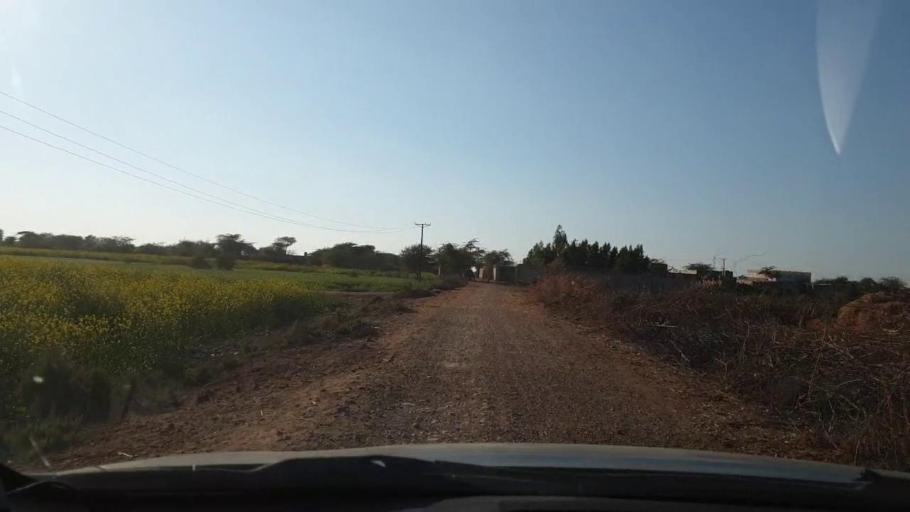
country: PK
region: Sindh
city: Jhol
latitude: 25.8690
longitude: 68.9480
